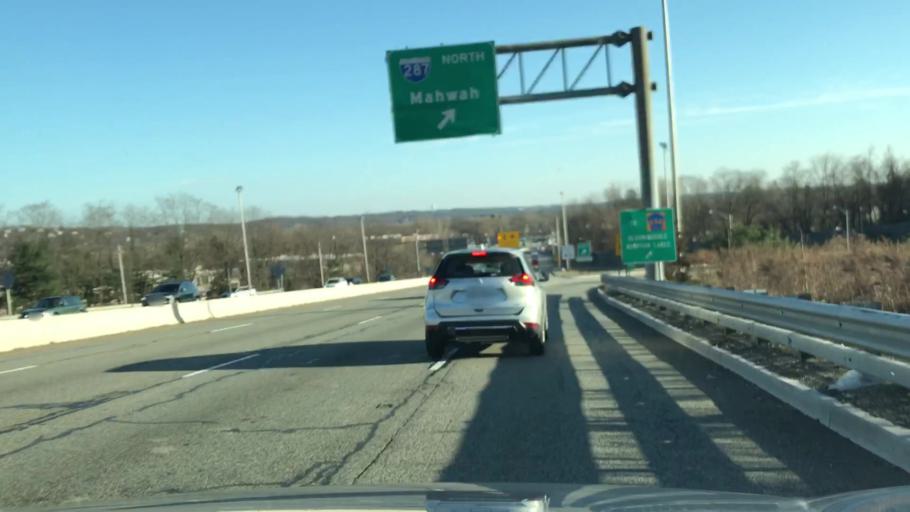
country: US
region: New Jersey
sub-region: Morris County
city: Riverdale
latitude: 40.9880
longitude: -74.3085
